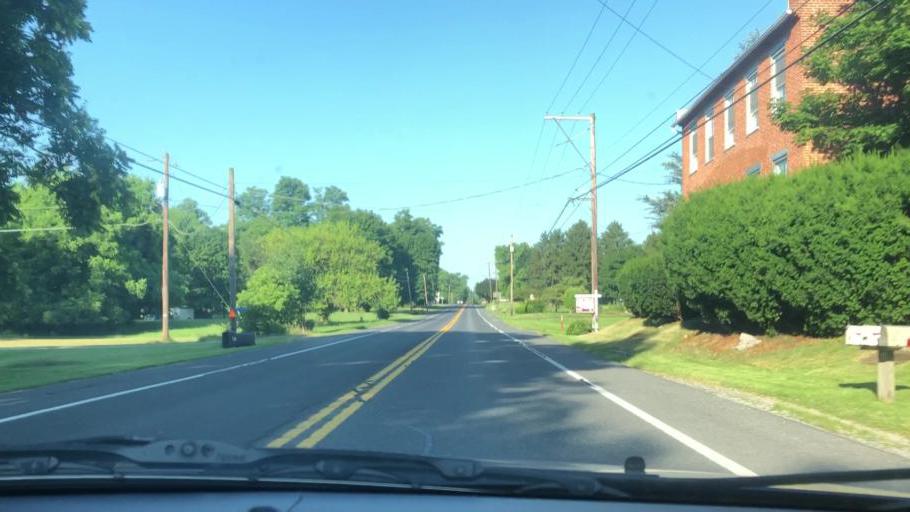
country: US
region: Pennsylvania
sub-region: Cumberland County
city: Carlisle
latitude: 40.1780
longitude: -77.2703
